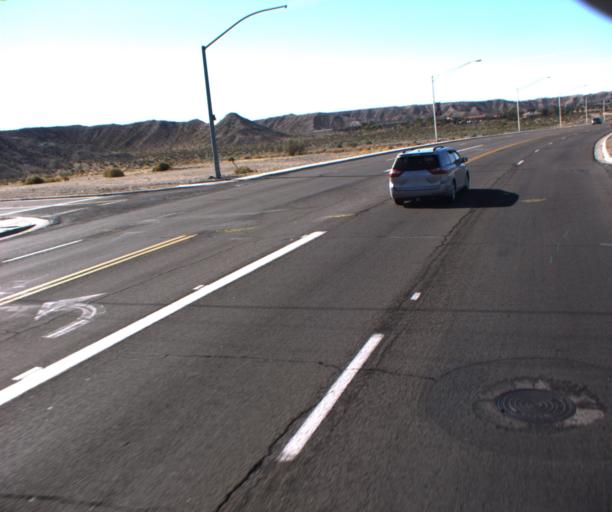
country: US
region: Arizona
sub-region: Mohave County
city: Bullhead City
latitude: 35.0699
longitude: -114.5895
